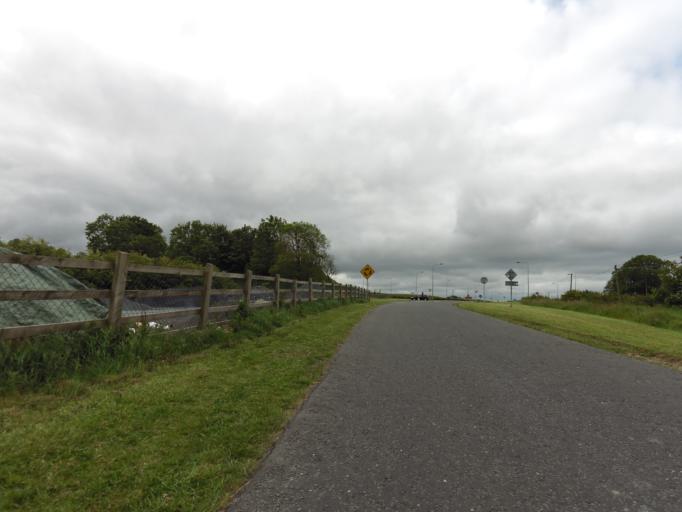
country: IE
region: Connaught
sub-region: County Galway
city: Athenry
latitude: 53.3116
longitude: -8.7533
